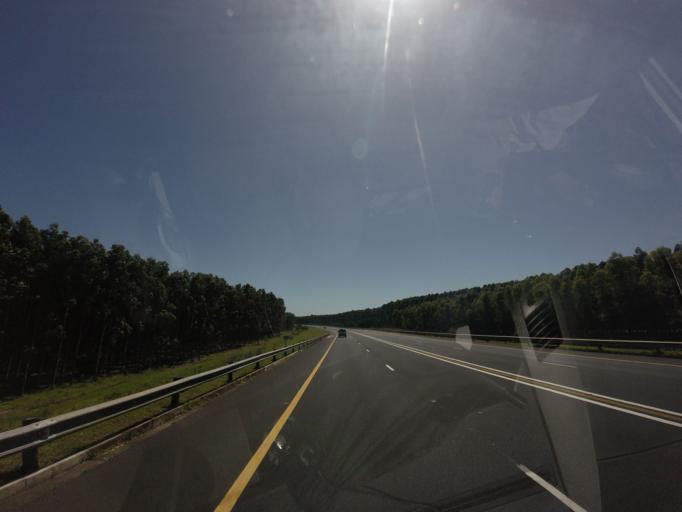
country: ZA
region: KwaZulu-Natal
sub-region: uThungulu District Municipality
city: Eshowe
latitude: -29.0221
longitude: 31.6703
